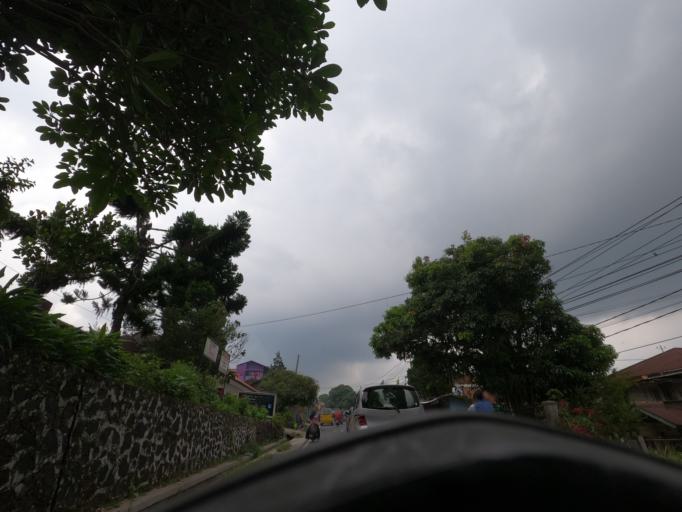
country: ID
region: West Java
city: Sukabumi
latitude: -6.7654
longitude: 107.0548
